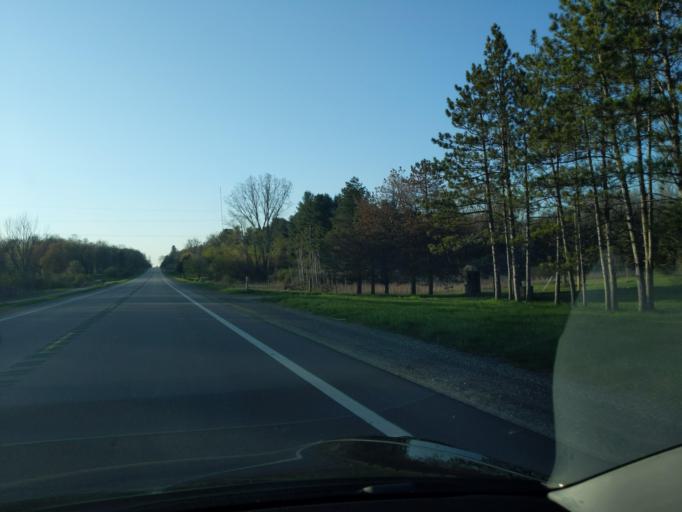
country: US
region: Michigan
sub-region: Washtenaw County
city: Chelsea
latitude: 42.3561
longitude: -84.0573
